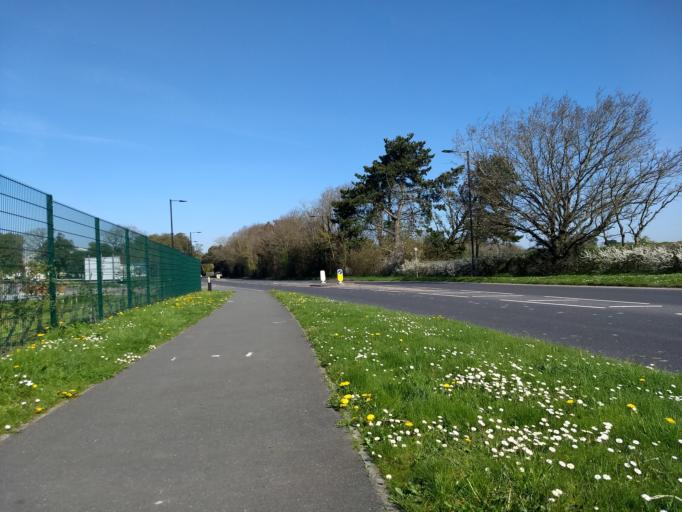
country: GB
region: England
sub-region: Isle of Wight
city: East Cowes
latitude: 50.7422
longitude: -1.2702
